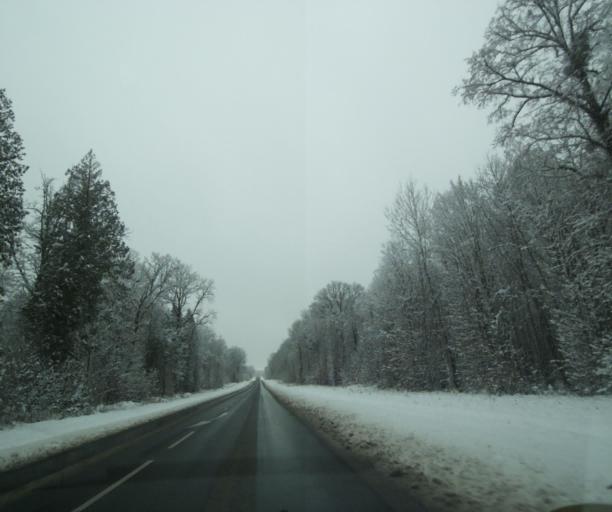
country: FR
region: Champagne-Ardenne
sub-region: Departement de la Haute-Marne
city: Laneuville-a-Remy
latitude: 48.5560
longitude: 4.8388
